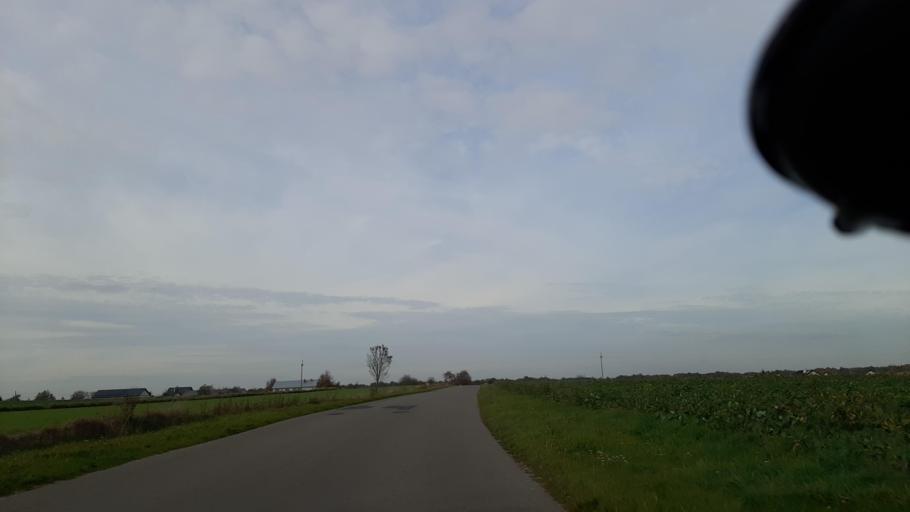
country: PL
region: Lublin Voivodeship
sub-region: Powiat lubelski
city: Garbow
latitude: 51.3853
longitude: 22.3716
